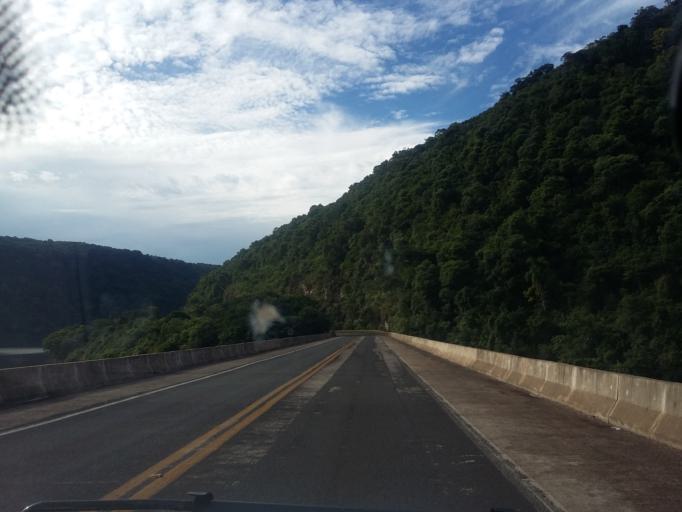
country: BR
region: Santa Catarina
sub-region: Celso Ramos
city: Celso Ramos
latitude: -27.6021
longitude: -51.4706
